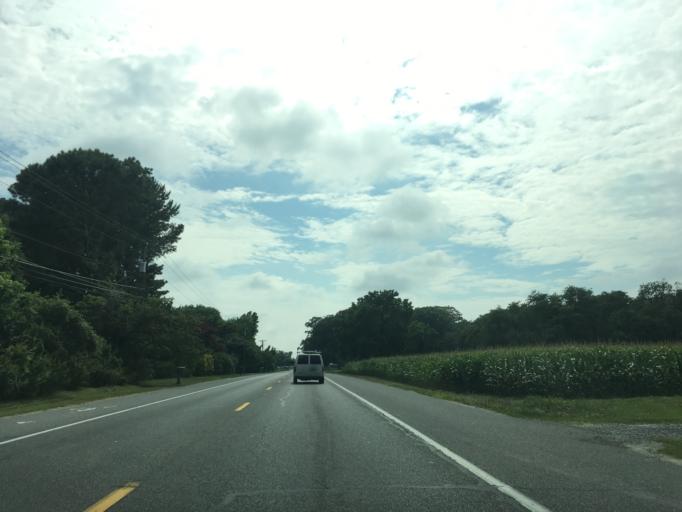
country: US
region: Delaware
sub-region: Sussex County
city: Millsboro
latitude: 38.5517
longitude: -75.2229
